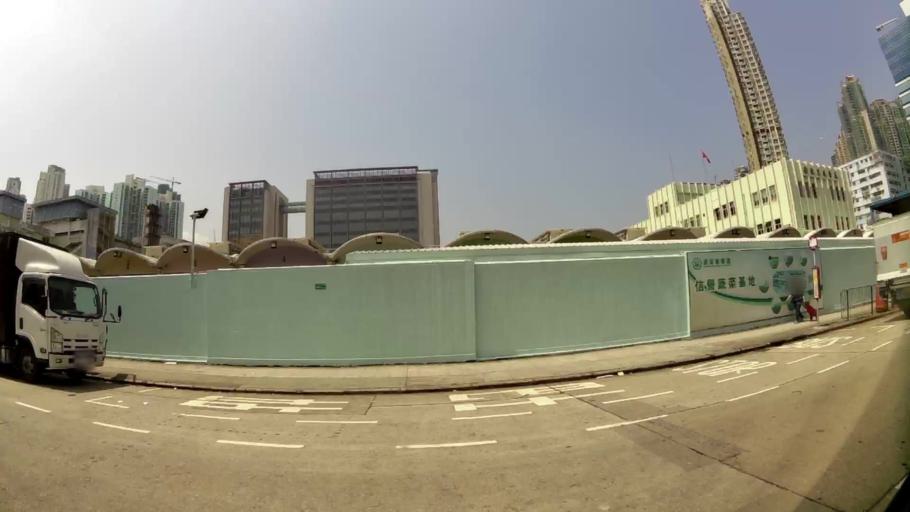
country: HK
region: Sham Shui Po
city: Sham Shui Po
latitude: 22.3332
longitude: 114.1544
